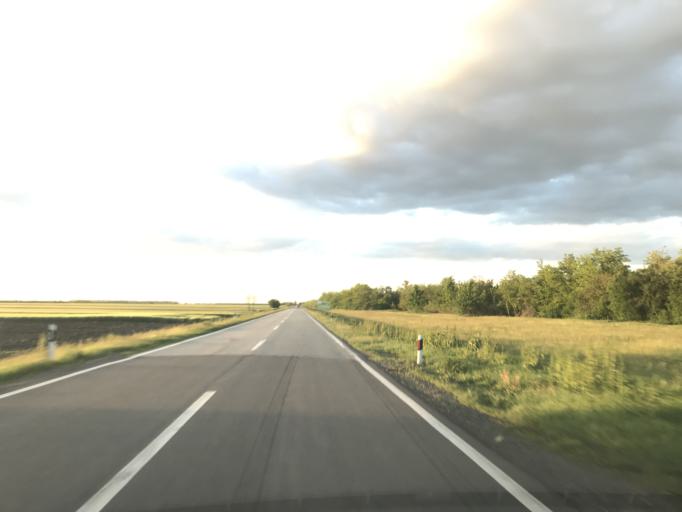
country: RS
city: Banatsko Karadordevo
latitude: 45.6141
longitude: 20.5731
